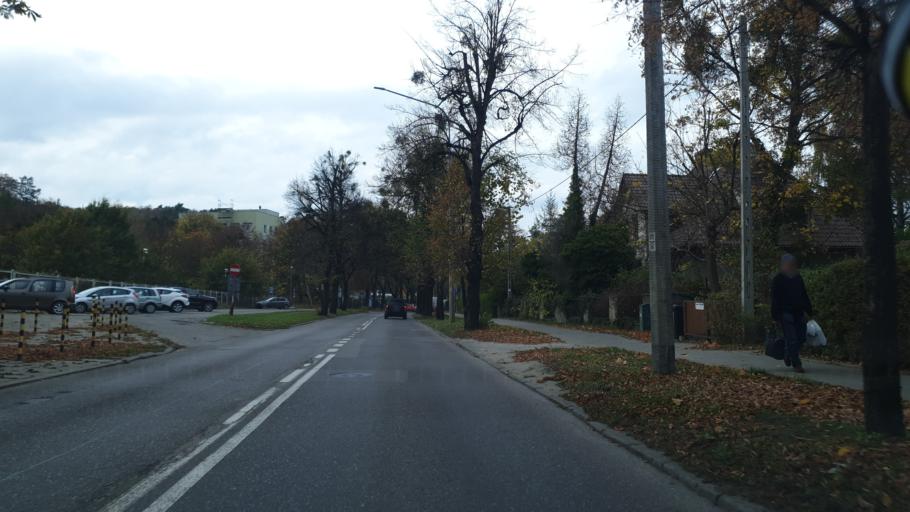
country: PL
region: Pomeranian Voivodeship
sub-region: Sopot
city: Sopot
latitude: 54.3941
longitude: 18.5674
